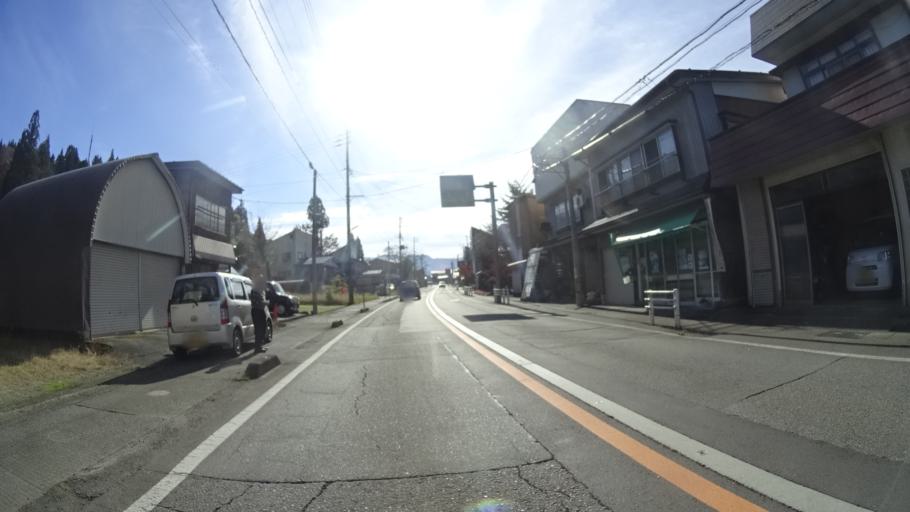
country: JP
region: Niigata
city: Muikamachi
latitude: 37.1624
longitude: 138.9684
